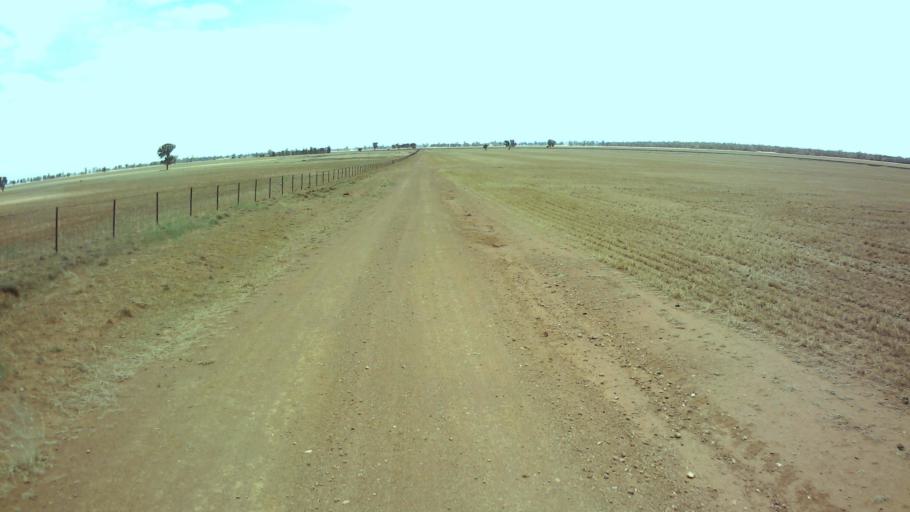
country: AU
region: New South Wales
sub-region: Weddin
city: Grenfell
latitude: -33.9041
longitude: 147.7385
